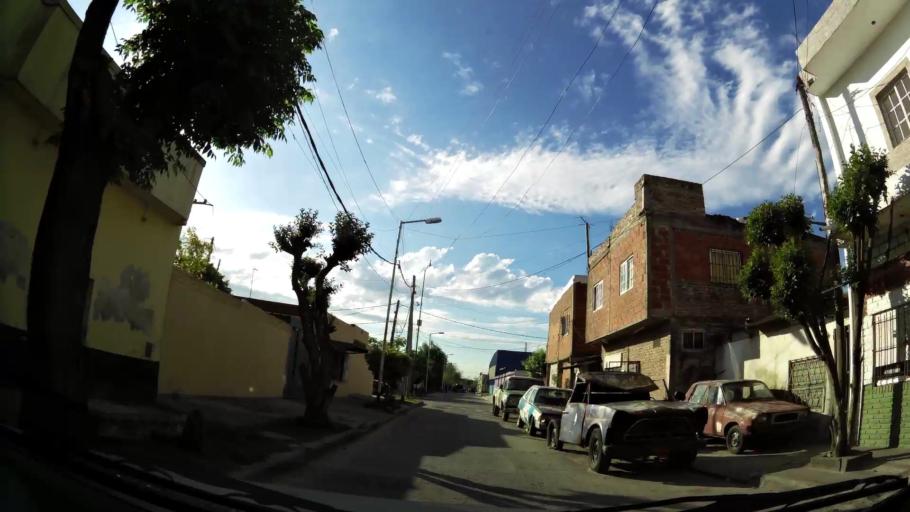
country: AR
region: Buenos Aires
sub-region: Partido de Avellaneda
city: Avellaneda
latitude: -34.6960
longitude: -58.3531
